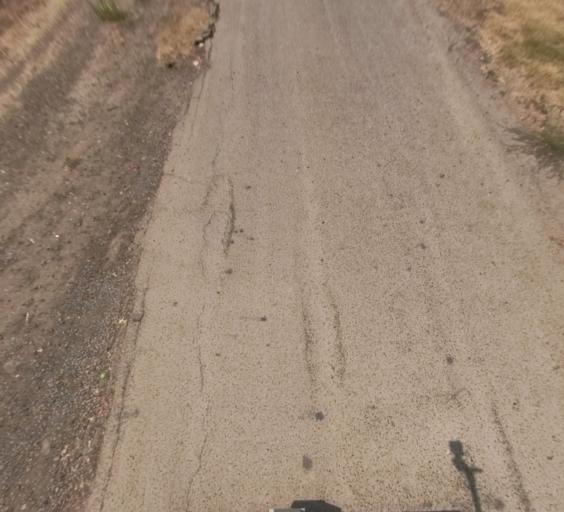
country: US
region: California
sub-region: Madera County
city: Fairmead
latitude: 37.0766
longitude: -120.1959
